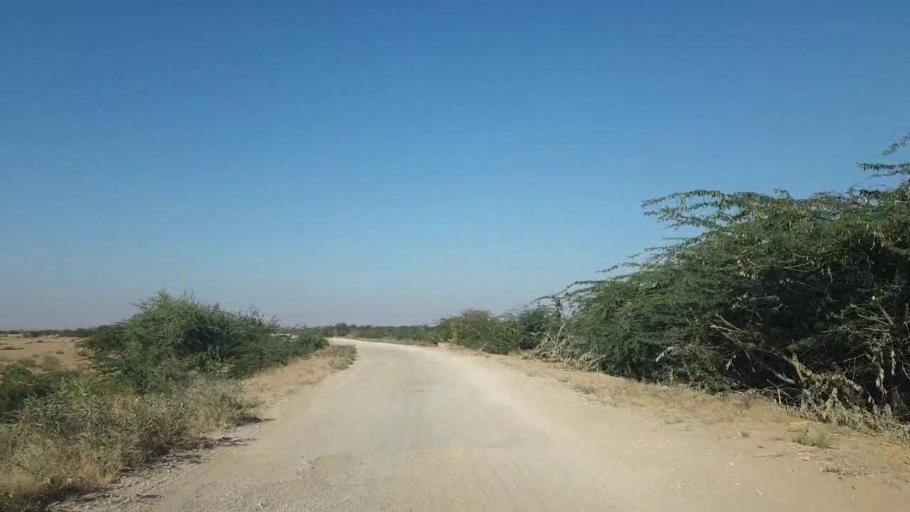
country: PK
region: Sindh
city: Malir Cantonment
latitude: 25.3314
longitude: 67.5720
